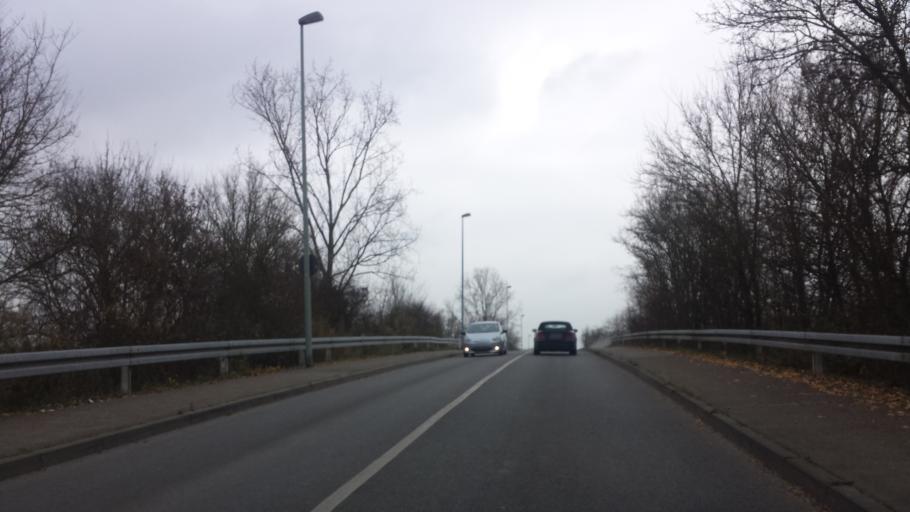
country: DE
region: Hesse
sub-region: Regierungsbezirk Darmstadt
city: Burstadt
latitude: 49.6412
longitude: 8.4757
